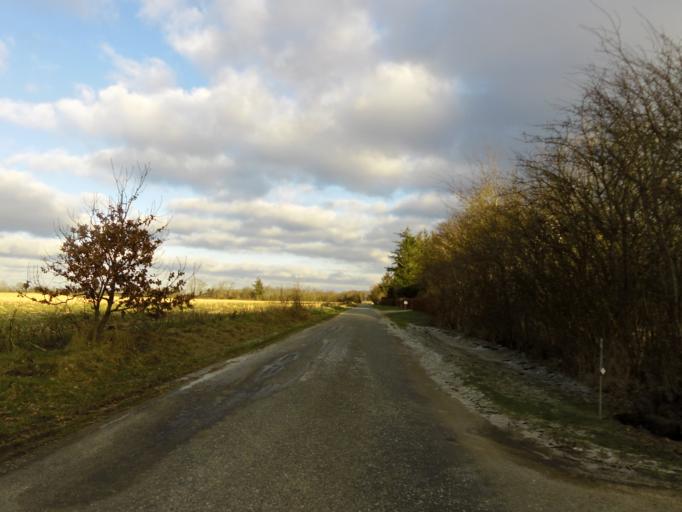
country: DK
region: South Denmark
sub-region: Esbjerg Kommune
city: Ribe
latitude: 55.2974
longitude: 8.8397
